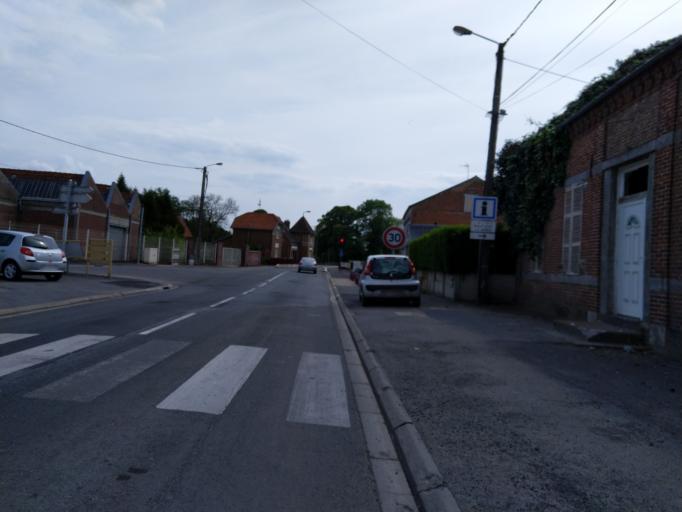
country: FR
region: Picardie
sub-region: Departement de l'Aisne
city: Boue
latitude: 50.0023
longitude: 3.6824
